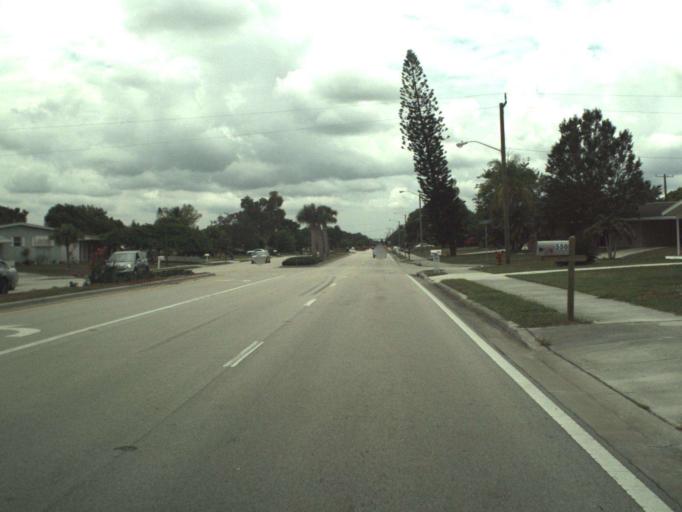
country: US
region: Florida
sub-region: Saint Lucie County
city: River Park
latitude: 27.3143
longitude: -80.3497
